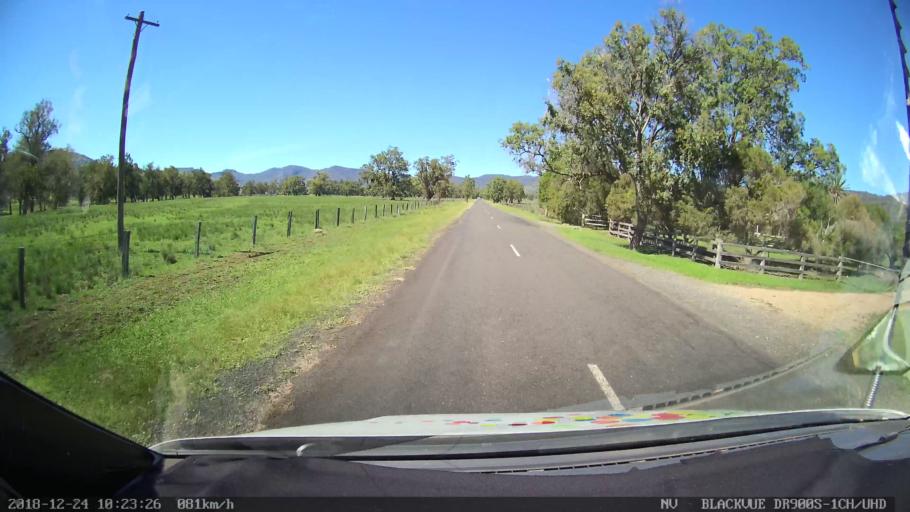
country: AU
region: New South Wales
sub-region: Liverpool Plains
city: Quirindi
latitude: -31.7751
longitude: 150.5380
